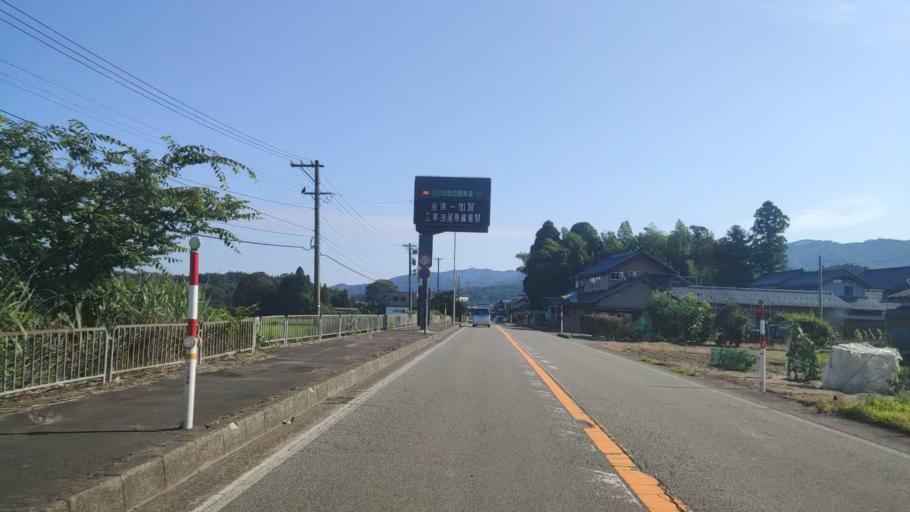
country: JP
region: Fukui
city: Maruoka
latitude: 36.2303
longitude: 136.2859
